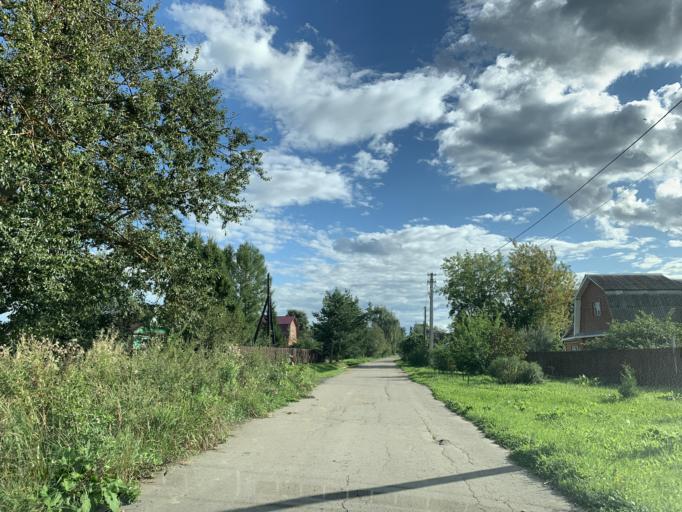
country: RU
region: Jaroslavl
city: Tunoshna
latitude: 57.6652
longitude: 40.0715
